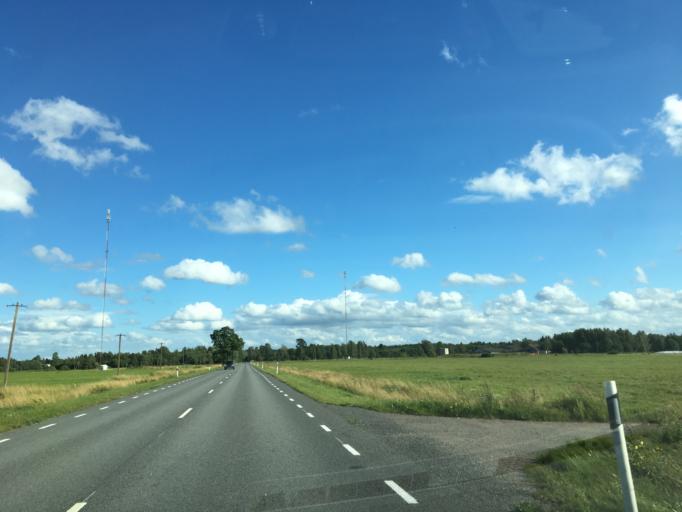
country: EE
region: Paernumaa
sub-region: Vaendra vald (alev)
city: Vandra
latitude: 58.5798
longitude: 25.1858
